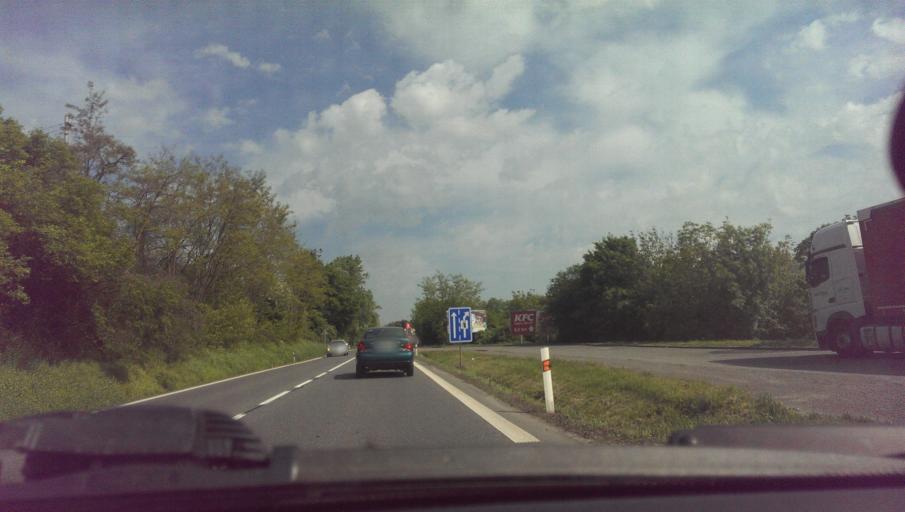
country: CZ
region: Zlin
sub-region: Okres Zlin
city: Napajedla
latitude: 49.1588
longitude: 17.5048
